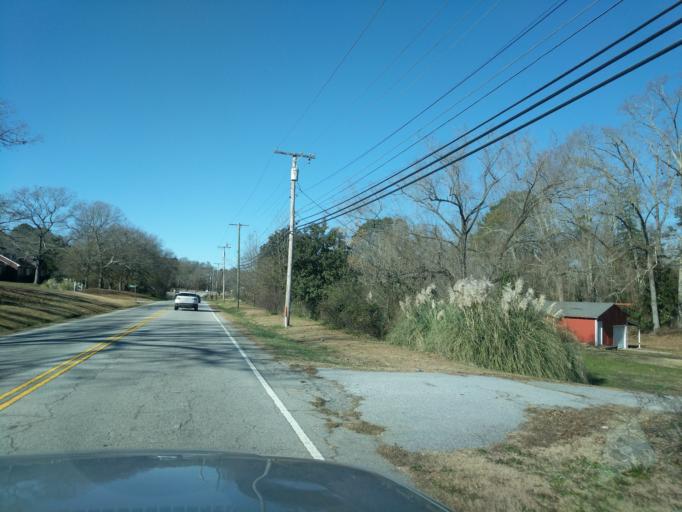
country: US
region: South Carolina
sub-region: Oconee County
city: Westminster
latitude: 34.6717
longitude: -83.1065
